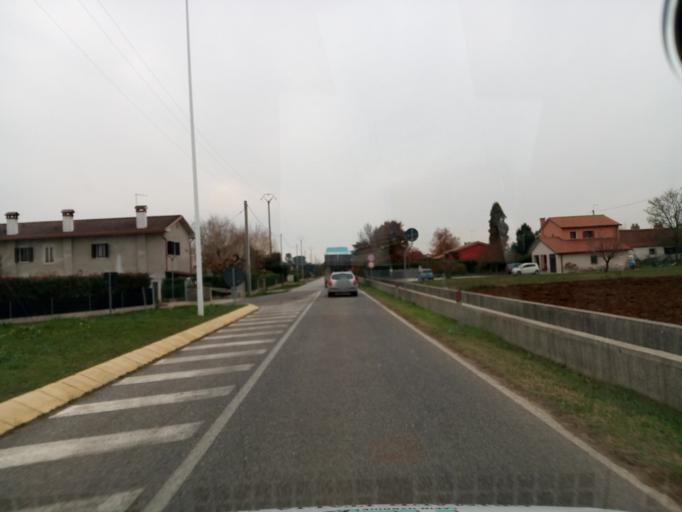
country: IT
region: Veneto
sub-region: Provincia di Treviso
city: Vedelago
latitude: 45.7054
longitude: 12.0166
